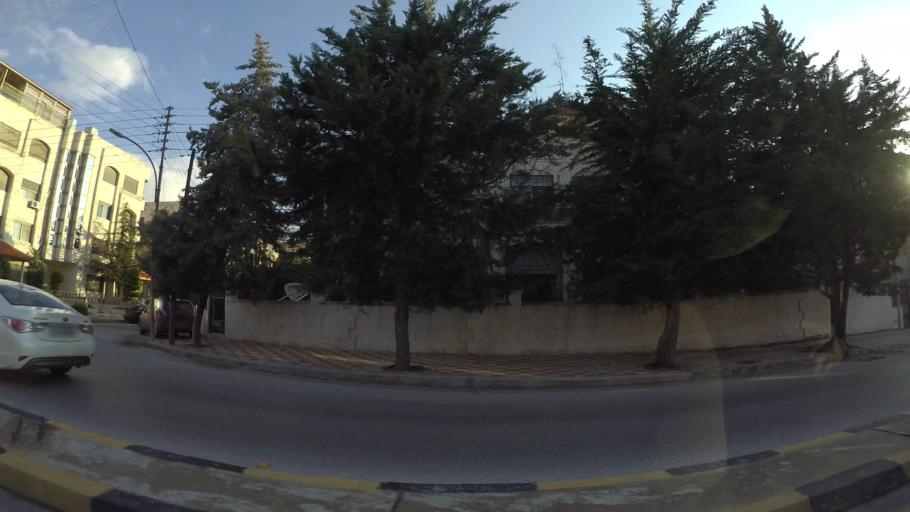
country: JO
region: Amman
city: Al Jubayhah
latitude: 31.9742
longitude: 35.8749
